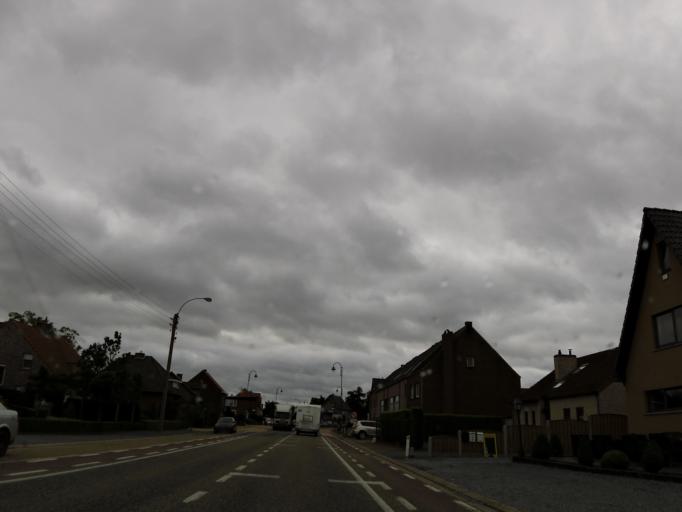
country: BE
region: Flanders
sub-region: Provincie Limburg
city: Kinrooi
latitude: 51.0957
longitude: 5.6985
